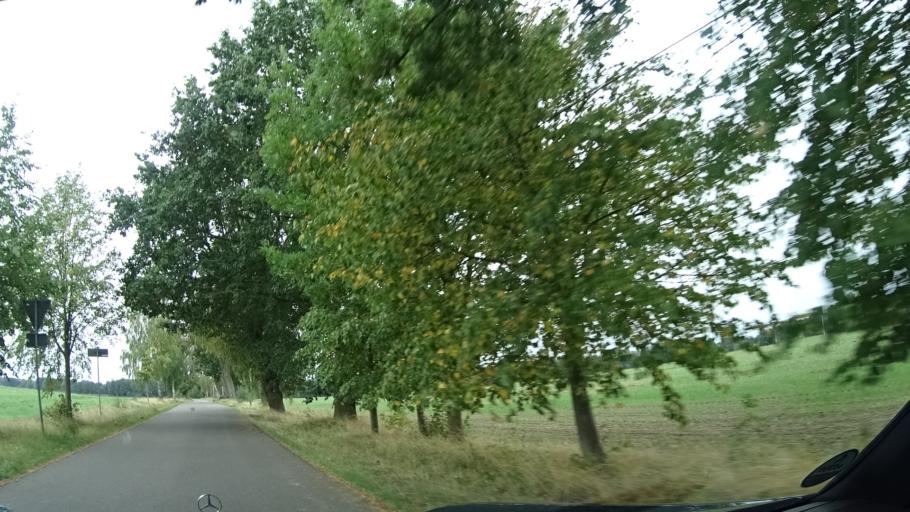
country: DE
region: Brandenburg
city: Neuruppin
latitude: 52.9658
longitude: 12.7606
